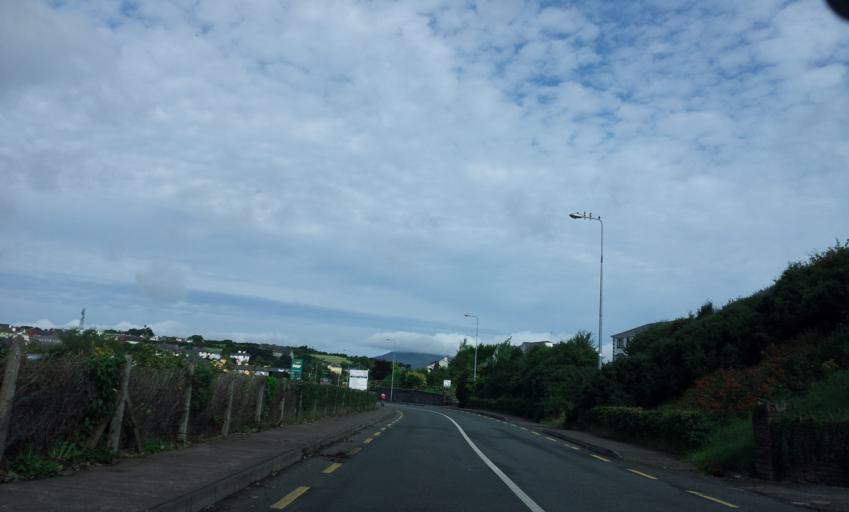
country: IE
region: Munster
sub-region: Ciarrai
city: Killorglin
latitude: 52.1041
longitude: -9.7789
